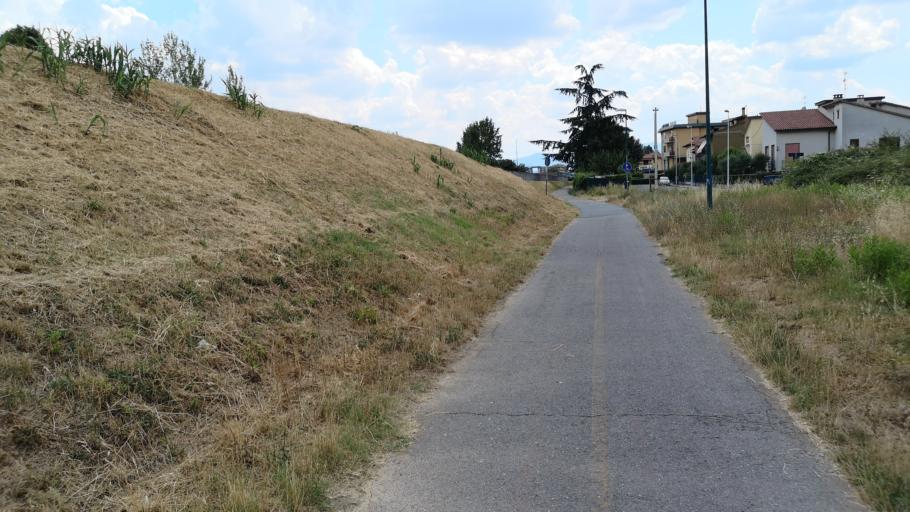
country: IT
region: Tuscany
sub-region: Provincia di Prato
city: Fornacelle
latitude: 43.8979
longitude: 11.0624
